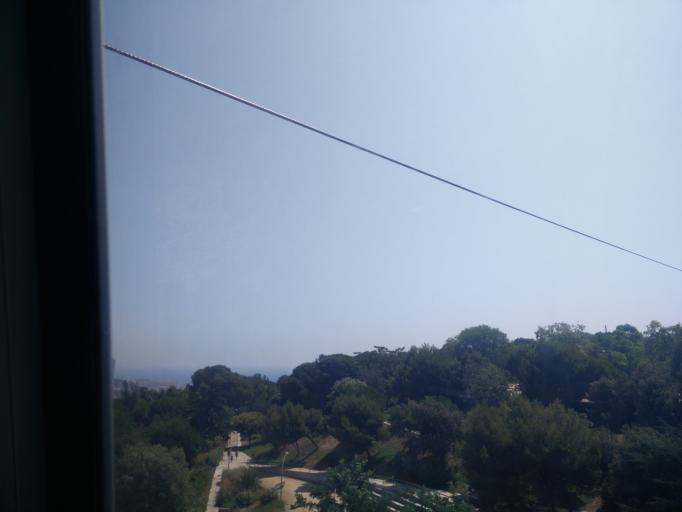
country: ES
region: Catalonia
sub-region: Provincia de Barcelona
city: Sants-Montjuic
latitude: 41.3680
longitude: 2.1660
